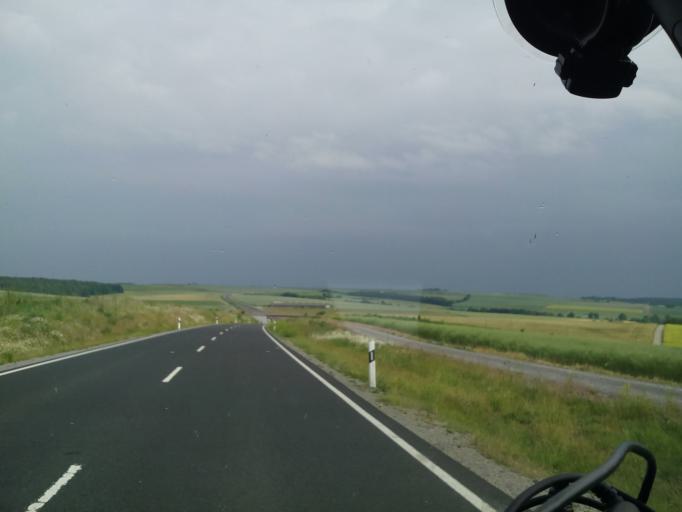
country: DE
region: Bavaria
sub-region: Regierungsbezirk Unterfranken
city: Mellrichstadt
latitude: 50.4372
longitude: 10.3224
